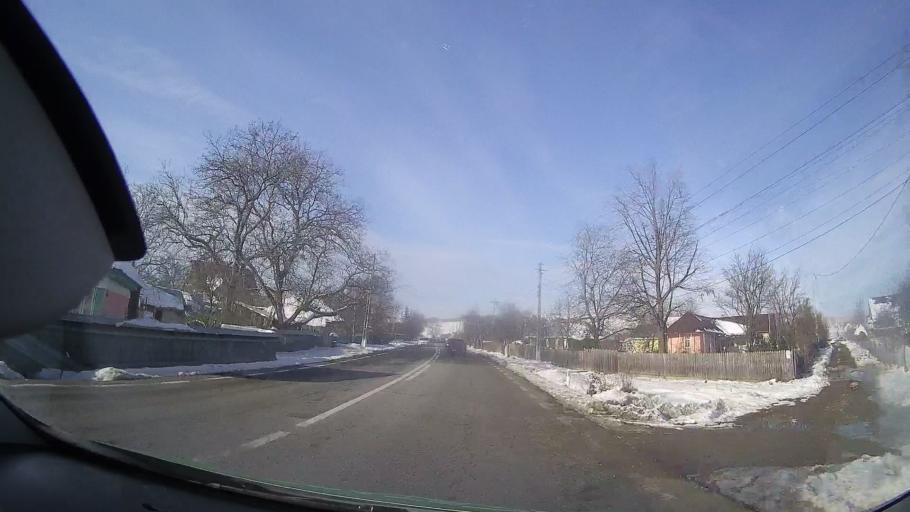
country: RO
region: Neamt
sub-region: Comuna Dobreni
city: Dobreni
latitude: 46.9956
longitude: 26.3914
